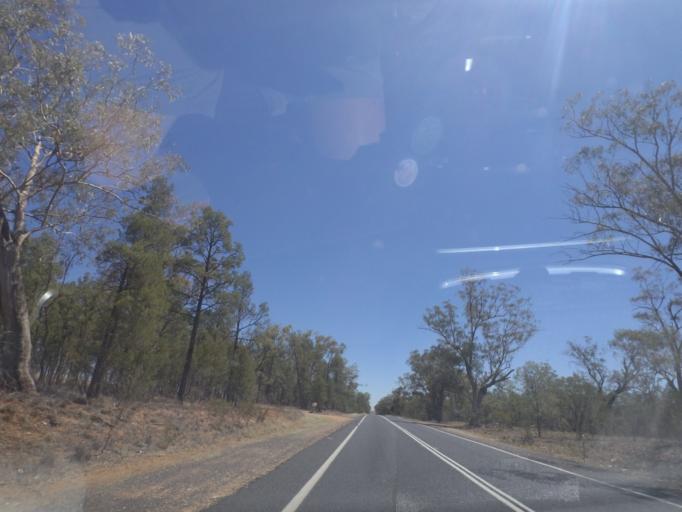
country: AU
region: New South Wales
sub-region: Gilgandra
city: Gilgandra
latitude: -31.4809
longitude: 148.8875
